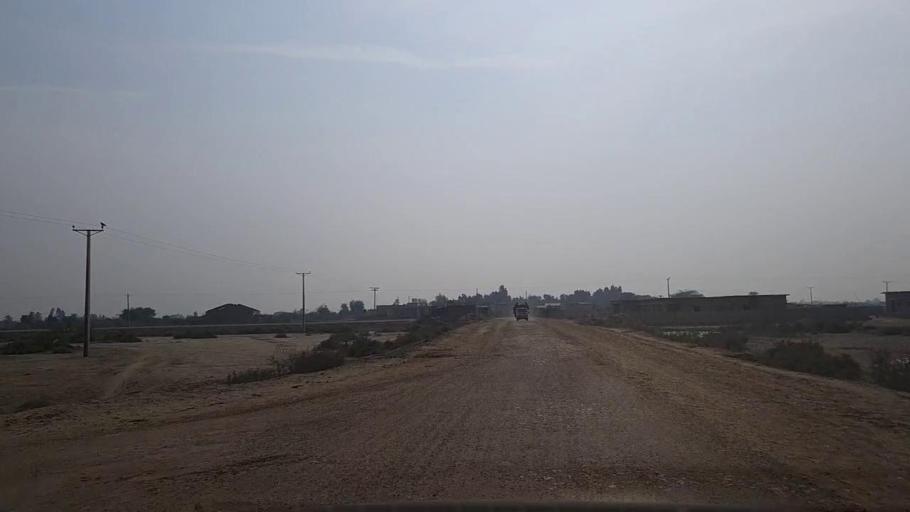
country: PK
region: Sindh
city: Mirpur Sakro
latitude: 24.4040
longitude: 67.7430
